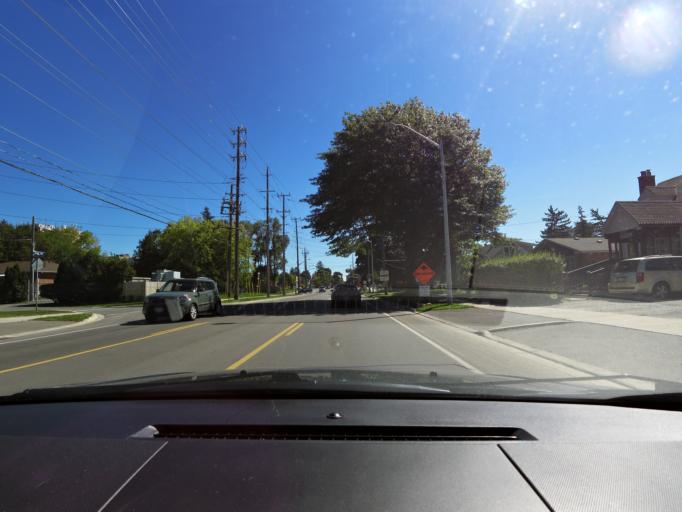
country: CA
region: Ontario
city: Burlington
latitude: 43.3228
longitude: -79.8341
